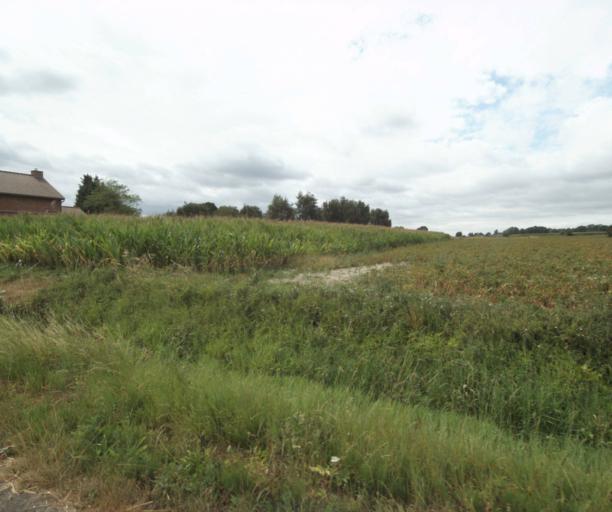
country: FR
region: Nord-Pas-de-Calais
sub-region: Departement du Nord
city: Roncq
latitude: 50.7367
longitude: 3.1045
